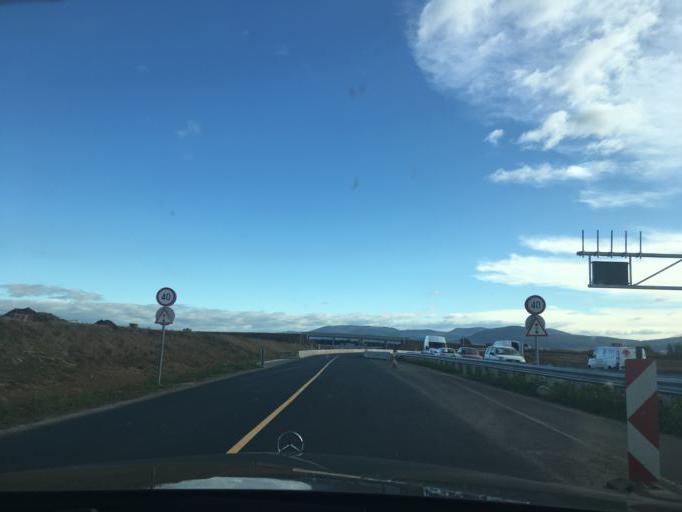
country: HU
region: Borsod-Abauj-Zemplen
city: Gonc
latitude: 48.5234
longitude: 21.2442
